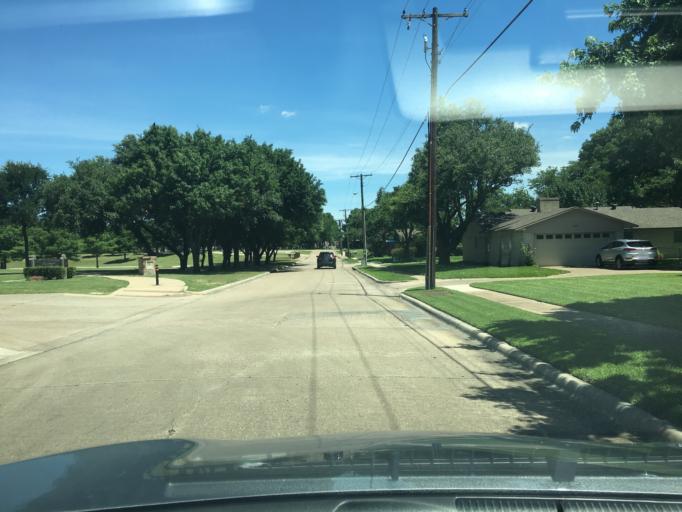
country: US
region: Texas
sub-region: Dallas County
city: Richardson
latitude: 32.9478
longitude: -96.6956
